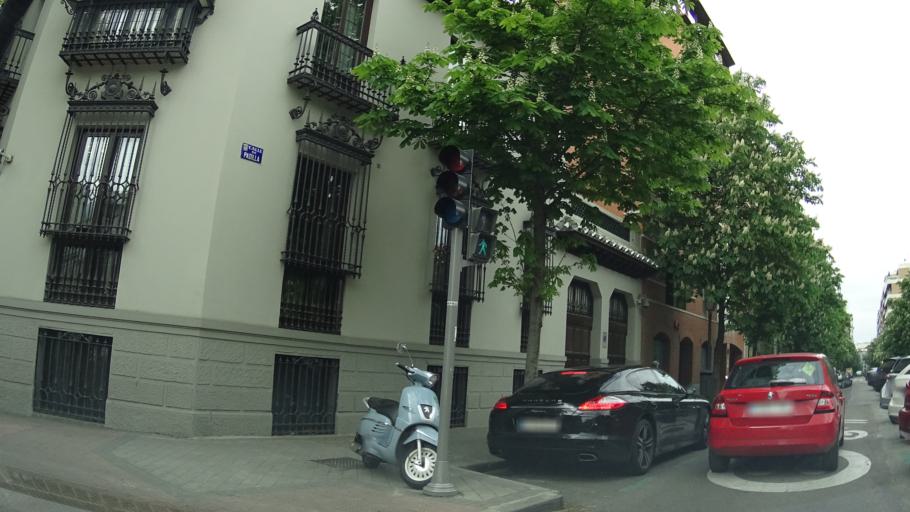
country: ES
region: Madrid
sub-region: Provincia de Madrid
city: Salamanca
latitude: 40.4314
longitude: -3.6798
